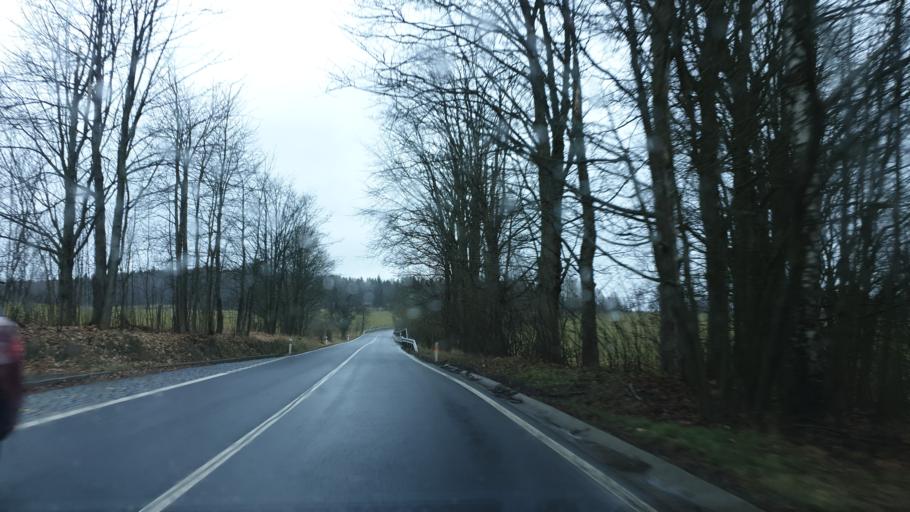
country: CZ
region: Karlovarsky
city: As
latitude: 50.2505
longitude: 12.1808
